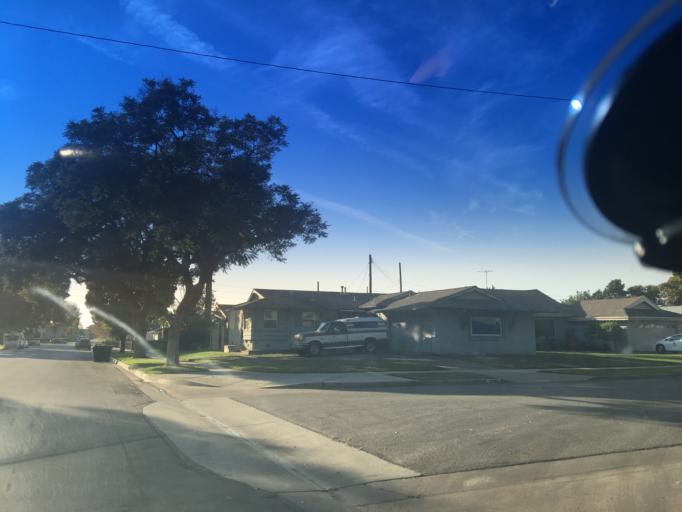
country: US
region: California
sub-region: Orange County
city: Anaheim
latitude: 33.8225
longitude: -117.8951
